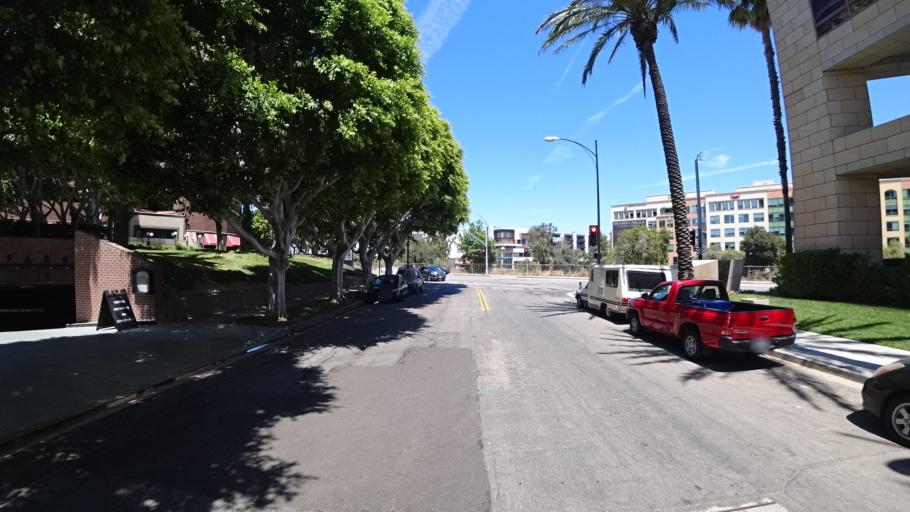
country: US
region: California
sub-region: Los Angeles County
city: Universal City
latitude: 34.1523
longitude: -118.3370
